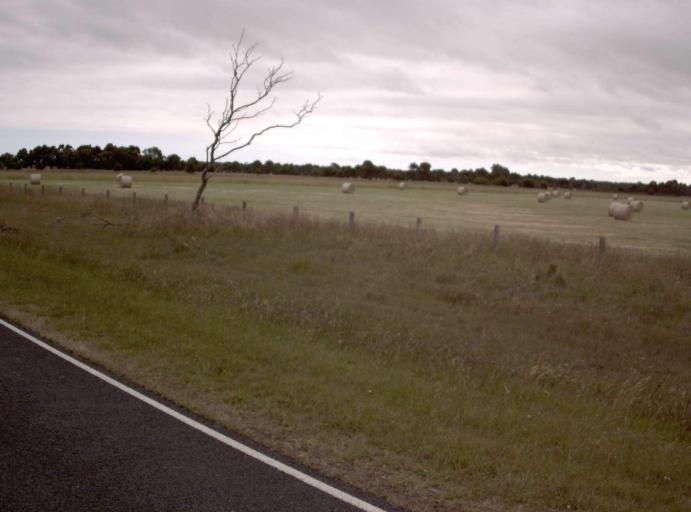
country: AU
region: Victoria
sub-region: Wellington
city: Sale
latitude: -38.5666
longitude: 146.8792
